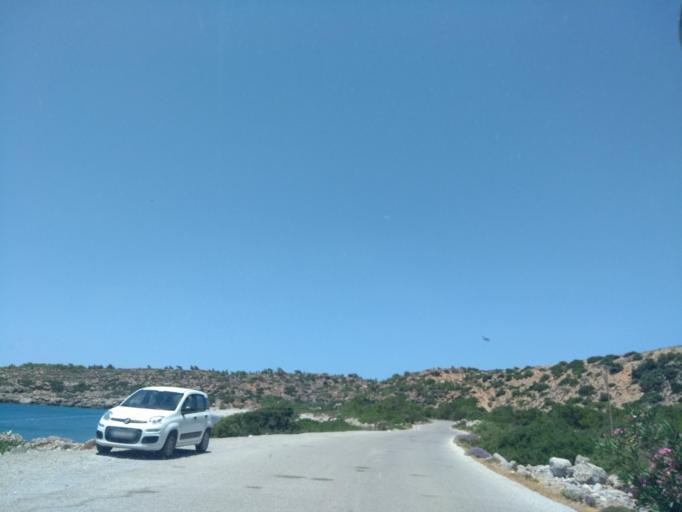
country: GR
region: Crete
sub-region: Nomos Chanias
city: Vryses
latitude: 35.3276
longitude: 23.5489
